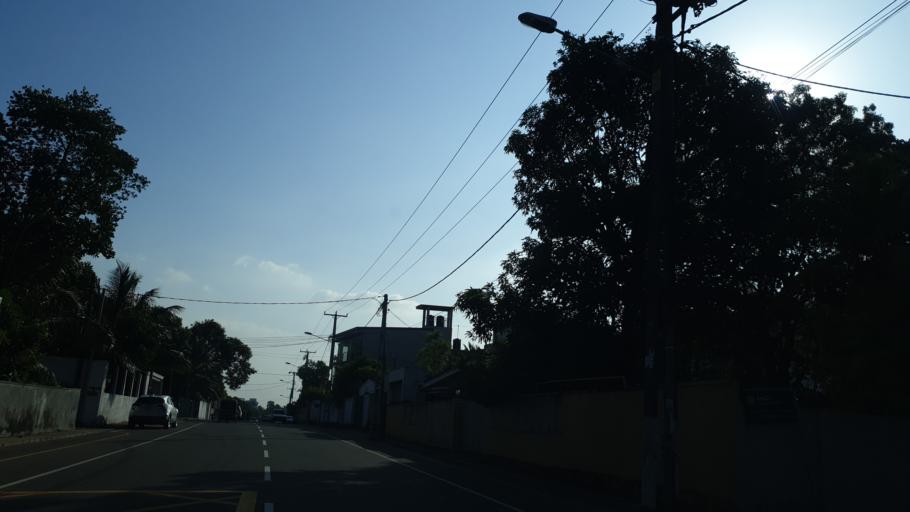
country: LK
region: Western
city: Sri Jayewardenepura Kotte
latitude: 6.8729
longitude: 79.8994
